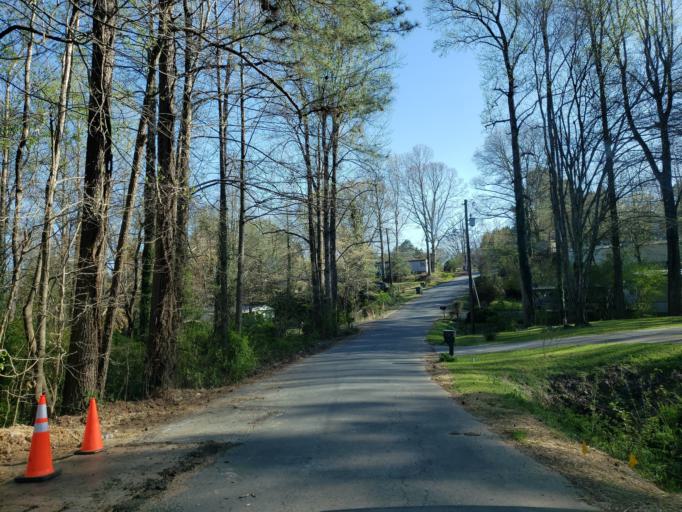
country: US
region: Georgia
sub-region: Cobb County
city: Kennesaw
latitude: 34.0365
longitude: -84.6018
